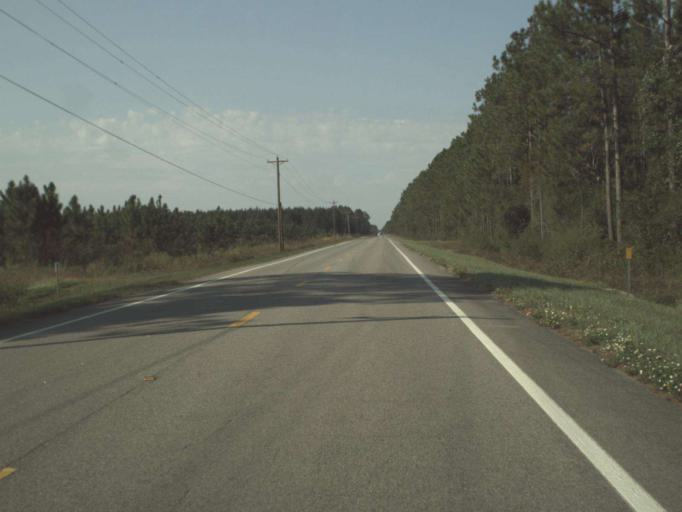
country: US
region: Florida
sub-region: Gulf County
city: Wewahitchka
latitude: 29.9826
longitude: -85.1672
